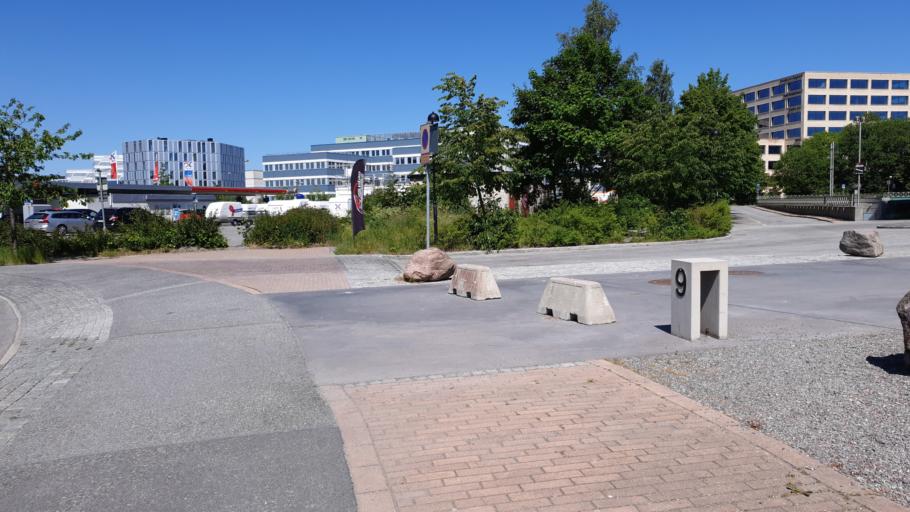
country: SE
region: Stockholm
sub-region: Sundbybergs Kommun
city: Sundbyberg
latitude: 59.3548
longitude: 17.9767
